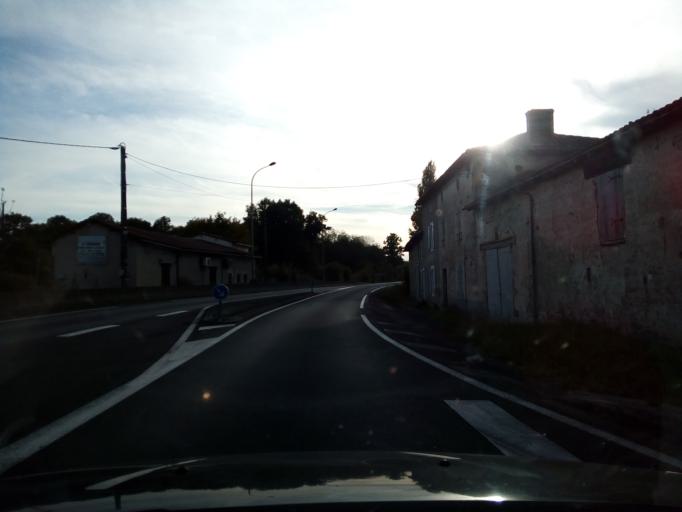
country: FR
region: Poitou-Charentes
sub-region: Departement de la Charente
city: Loubert
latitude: 45.9363
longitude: 0.5366
